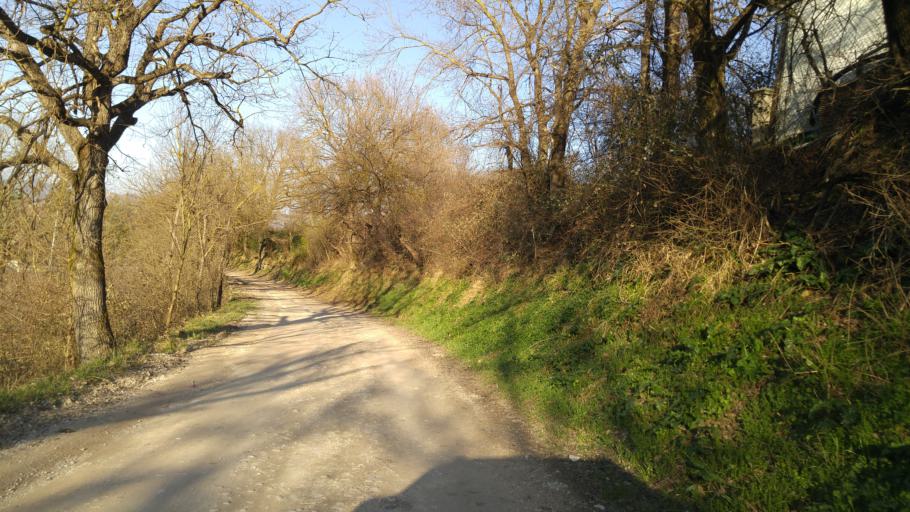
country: IT
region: The Marches
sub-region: Provincia di Pesaro e Urbino
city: Cagli
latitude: 43.5534
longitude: 12.6562
